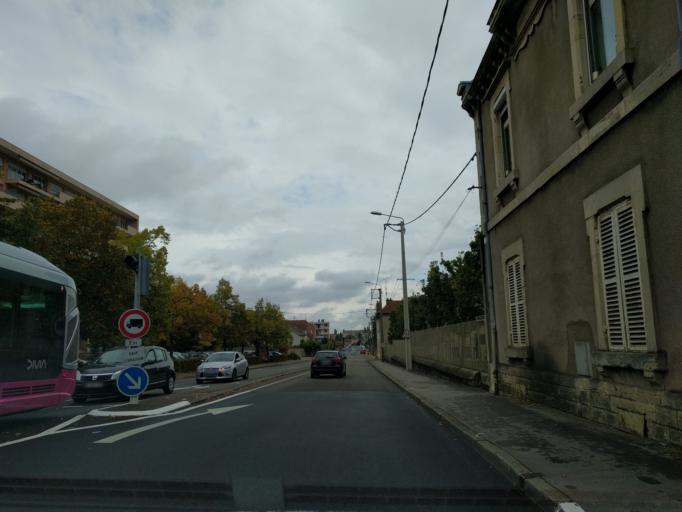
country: FR
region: Bourgogne
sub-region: Departement de la Cote-d'Or
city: Dijon
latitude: 47.3134
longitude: 5.0141
